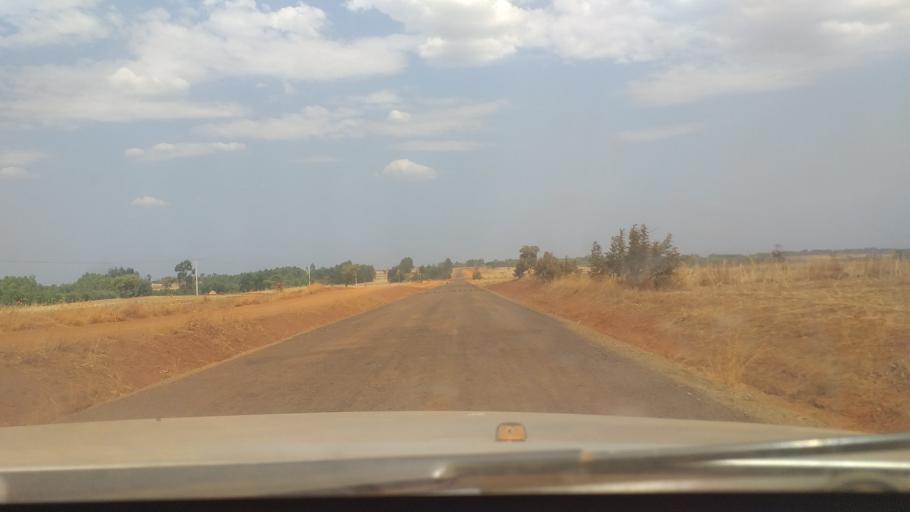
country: ET
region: Binshangul Gumuz
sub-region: Asosa
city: Asosa
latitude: 10.0785
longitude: 34.6425
